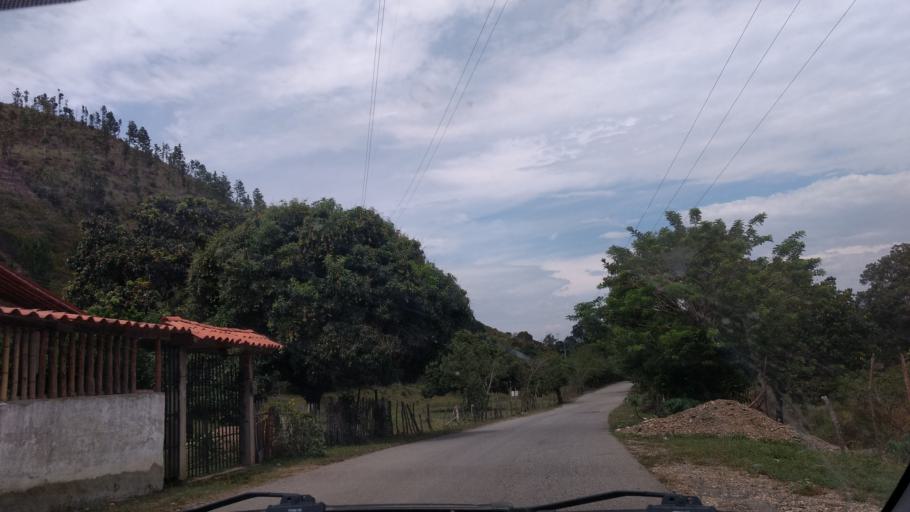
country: CO
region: Cauca
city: Buenos Aires
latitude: 3.0775
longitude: -76.6508
